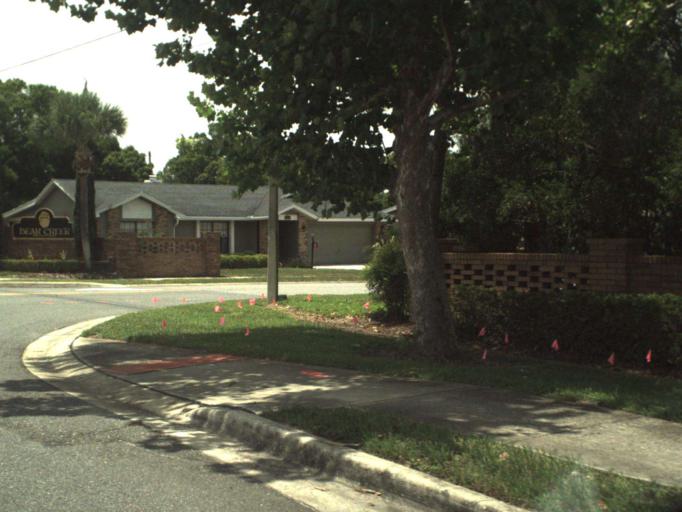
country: US
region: Florida
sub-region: Seminole County
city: Goldenrod
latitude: 28.6187
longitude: -81.2622
